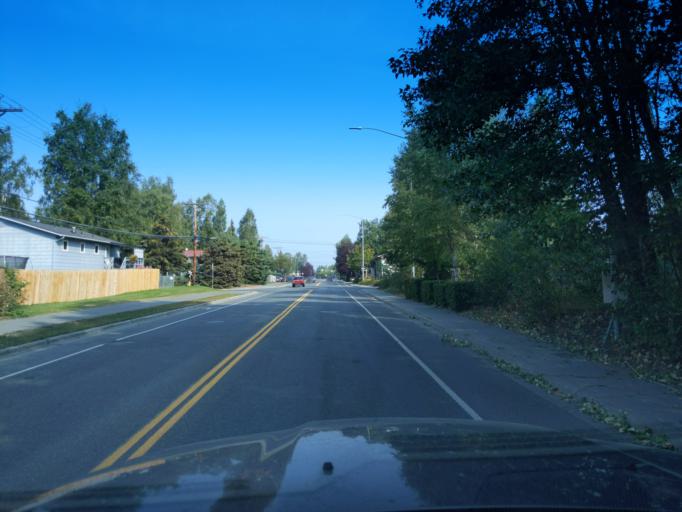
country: US
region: Alaska
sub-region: Anchorage Municipality
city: Anchorage
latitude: 61.1919
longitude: -149.9428
